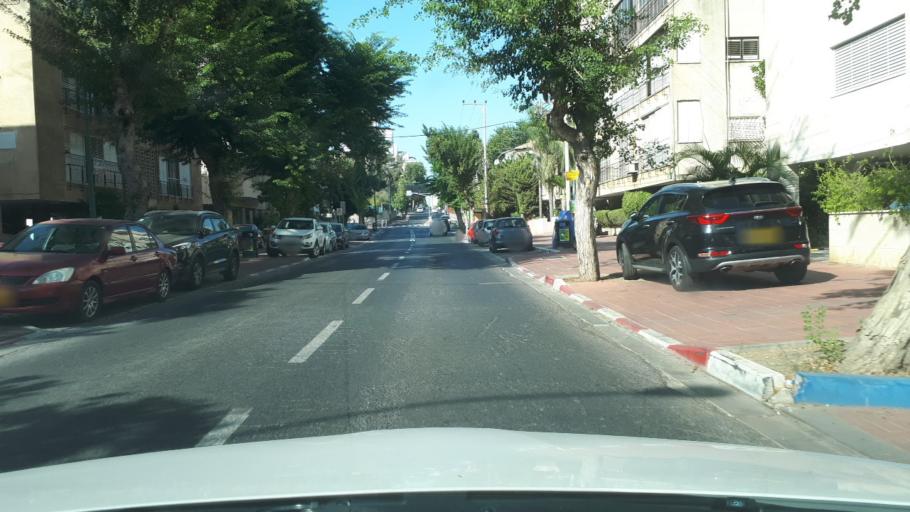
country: IL
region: Tel Aviv
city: Giv`atayim
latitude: 32.0649
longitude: 34.8237
